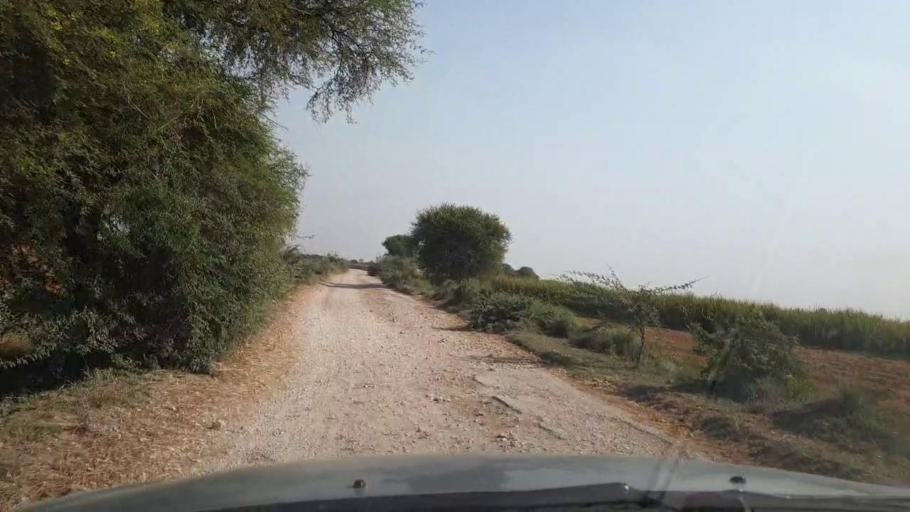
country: PK
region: Sindh
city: Bulri
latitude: 24.9199
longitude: 68.3545
